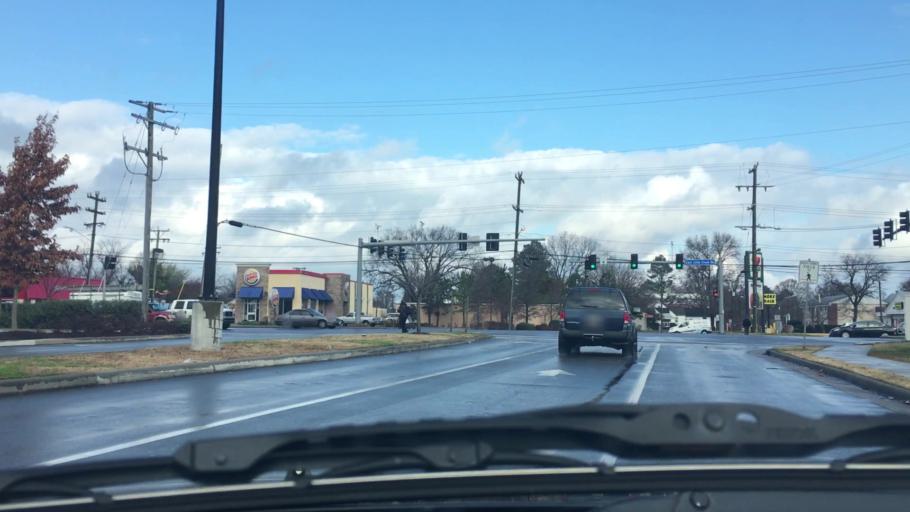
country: US
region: Virginia
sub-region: City of Norfolk
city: Norfolk
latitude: 36.9151
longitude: -76.2519
